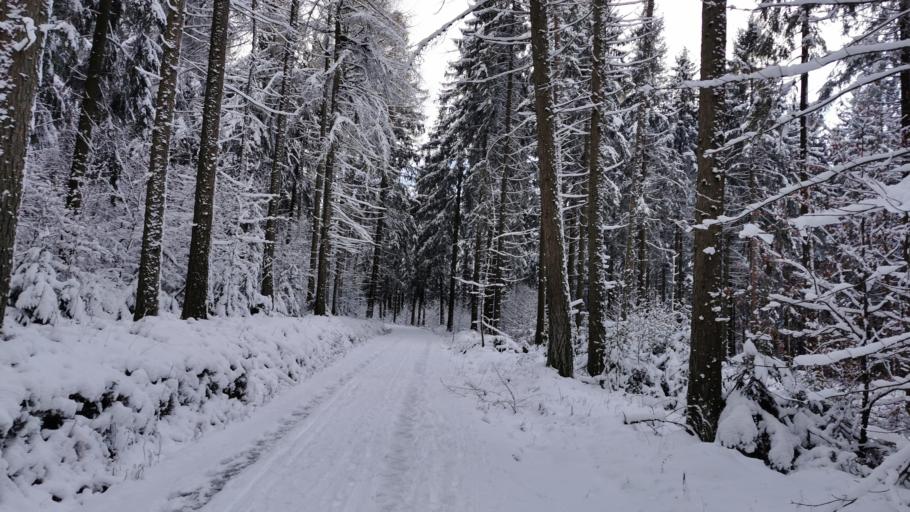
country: DE
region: Bavaria
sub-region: Upper Franconia
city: Reichenbach
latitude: 50.4613
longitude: 11.4483
